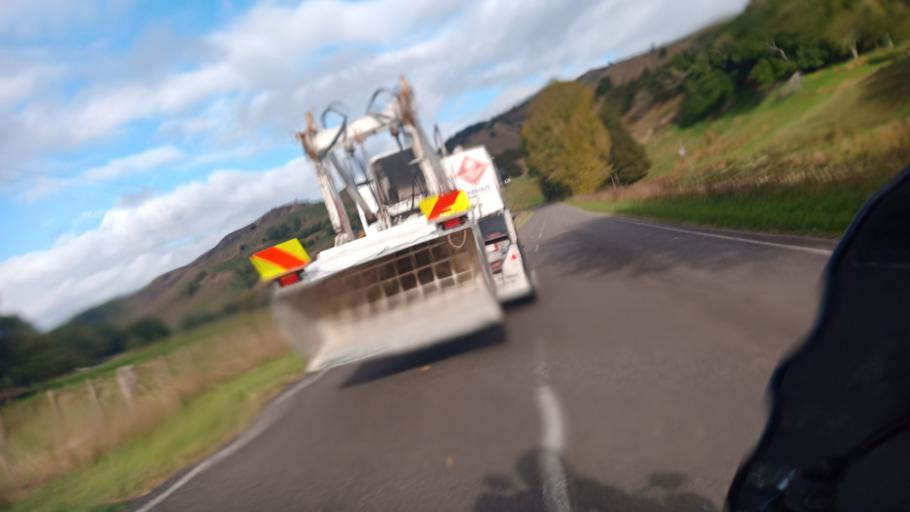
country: NZ
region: Gisborne
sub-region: Gisborne District
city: Gisborne
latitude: -38.5900
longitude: 177.7822
